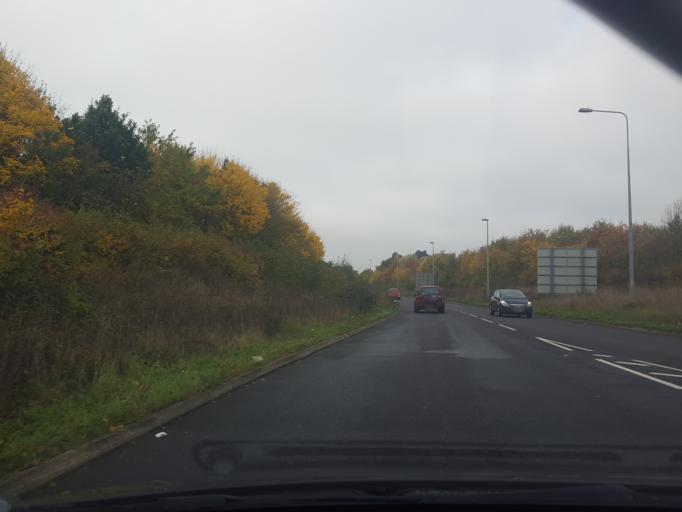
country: GB
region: England
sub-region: Essex
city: Little Clacton
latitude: 51.8193
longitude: 1.1356
